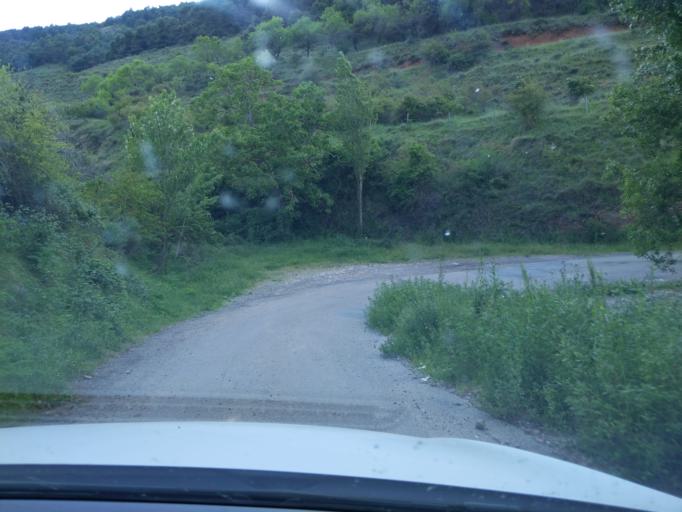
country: ES
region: La Rioja
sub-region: Provincia de La Rioja
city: Clavijo
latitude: 42.3482
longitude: -2.4299
